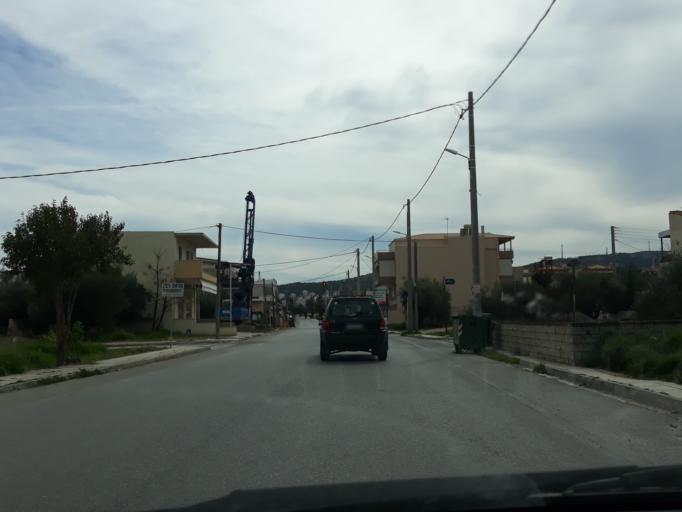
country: GR
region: Attica
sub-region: Nomarchia Dytikis Attikis
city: Ano Liosia
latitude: 38.0820
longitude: 23.7105
